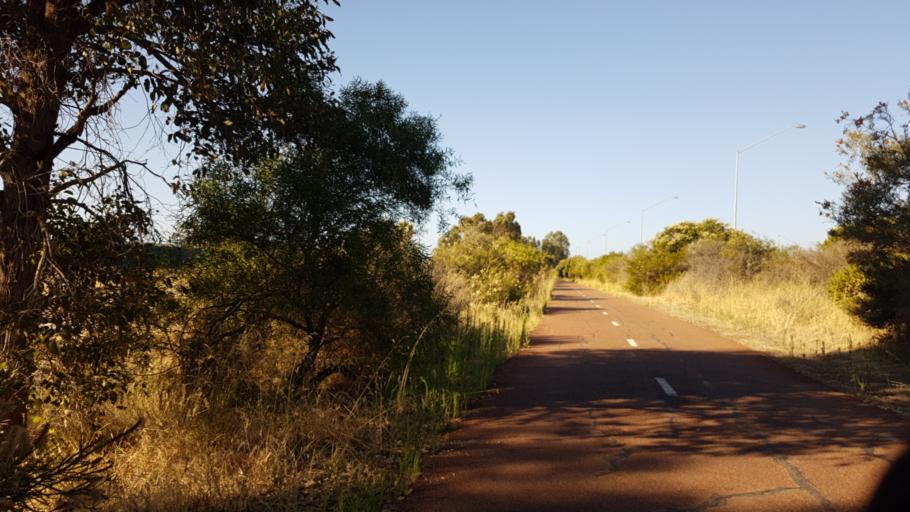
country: AU
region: Western Australia
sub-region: Kwinana
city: Wellard
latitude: -32.2911
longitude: 115.8358
